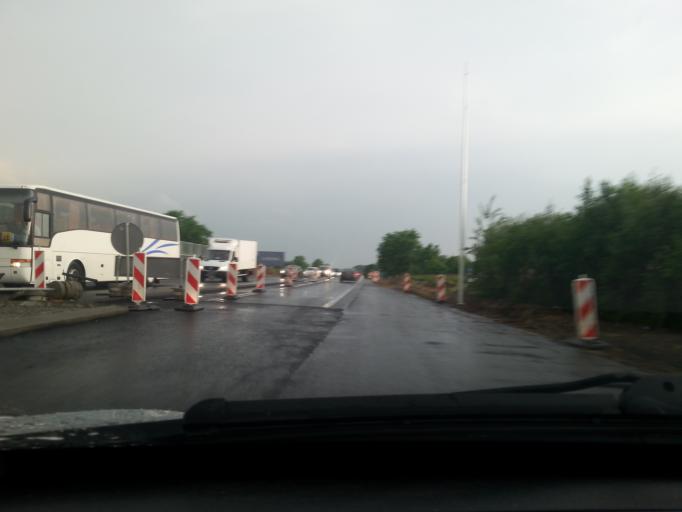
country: PL
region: Lodz Voivodeship
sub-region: Powiat zgierski
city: Strykow
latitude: 51.8766
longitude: 19.5776
